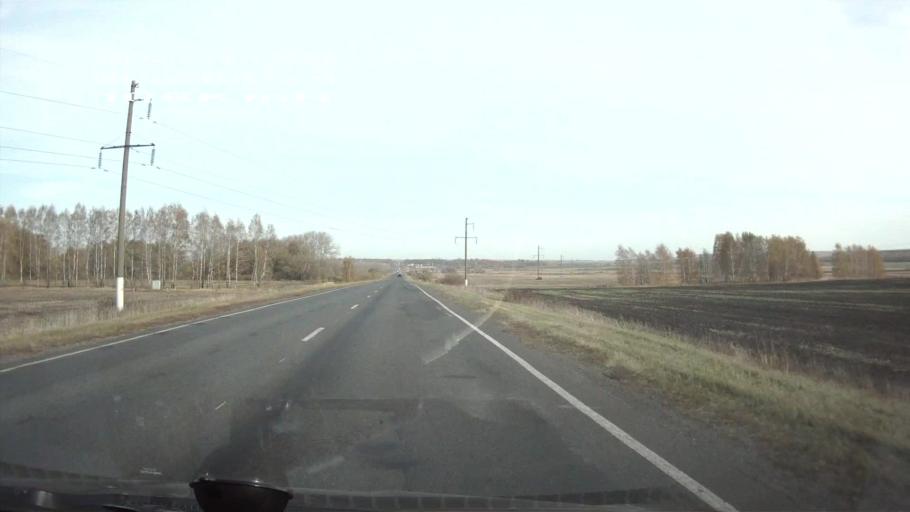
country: RU
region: Mordoviya
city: Atyashevo
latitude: 54.5447
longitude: 45.9430
